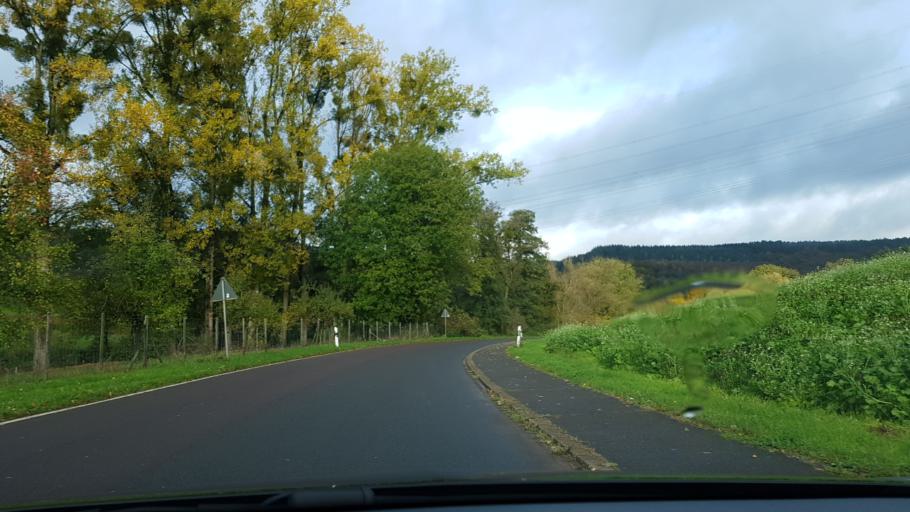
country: DE
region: Rheinland-Pfalz
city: Schweich
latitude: 49.8310
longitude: 6.7363
